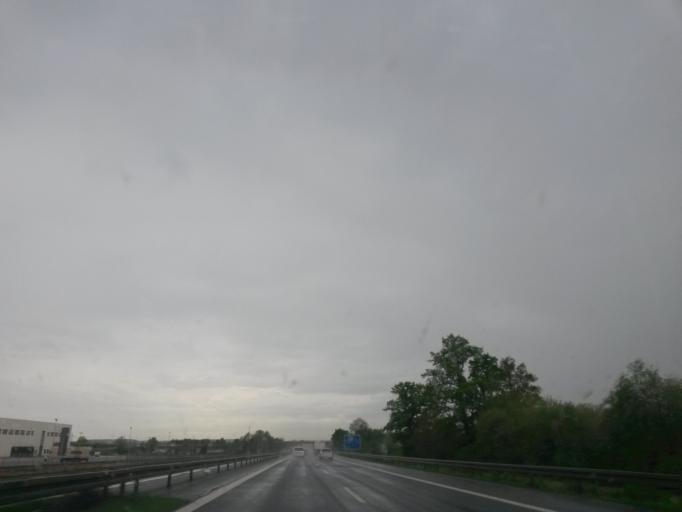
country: DE
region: Bavaria
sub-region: Upper Franconia
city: Forchheim
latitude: 49.6905
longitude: 11.0597
